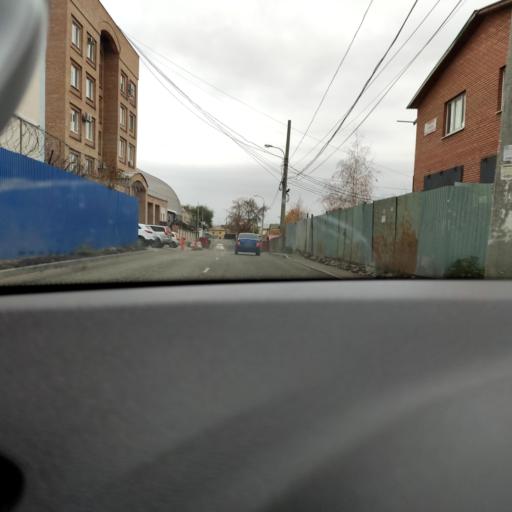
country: RU
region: Samara
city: Samara
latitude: 53.1792
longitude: 50.1417
